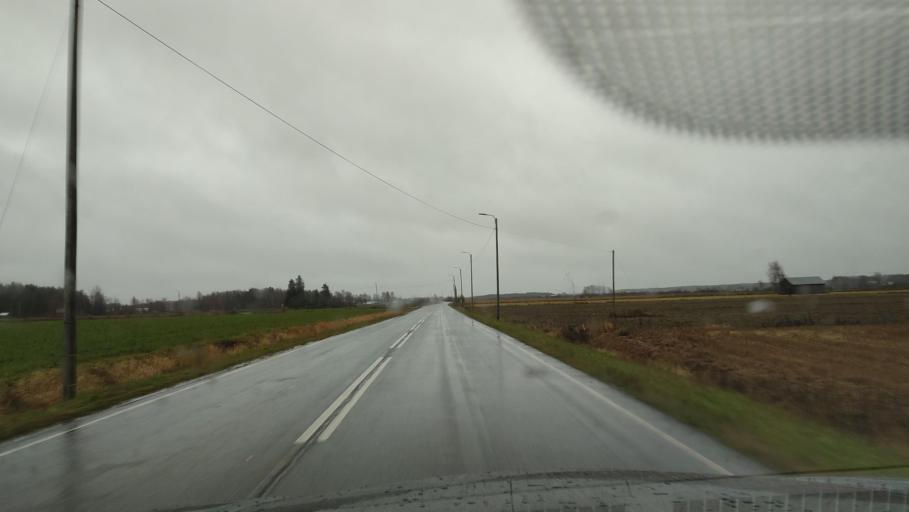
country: FI
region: Ostrobothnia
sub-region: Vaasa
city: Ristinummi
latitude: 63.0472
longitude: 21.7420
